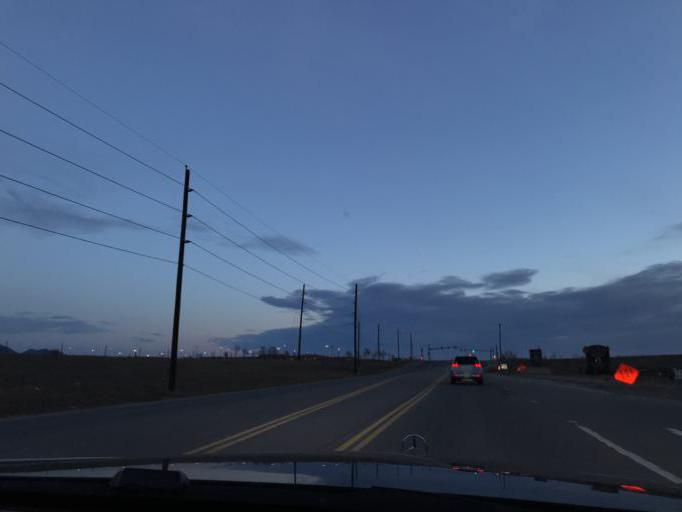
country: US
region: Colorado
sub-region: Jefferson County
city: Arvada
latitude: 39.8565
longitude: -105.1653
